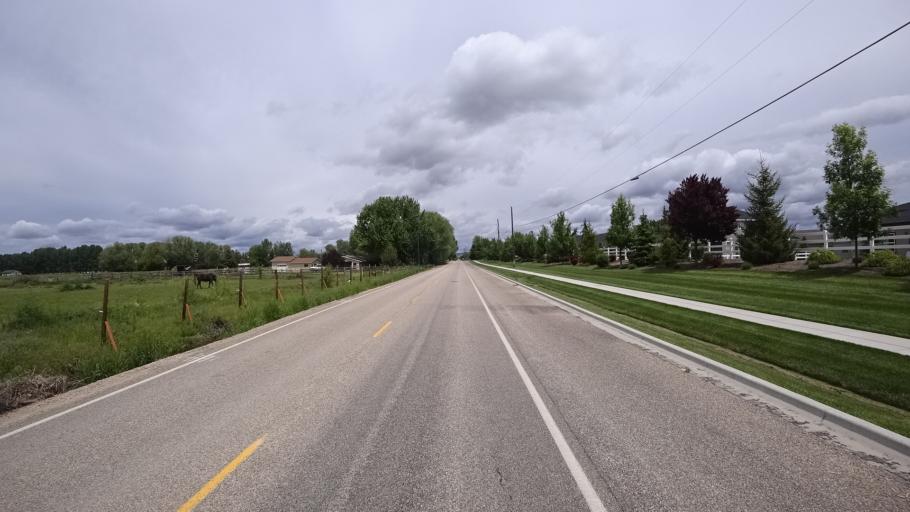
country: US
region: Idaho
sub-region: Ada County
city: Eagle
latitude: 43.7136
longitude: -116.4035
